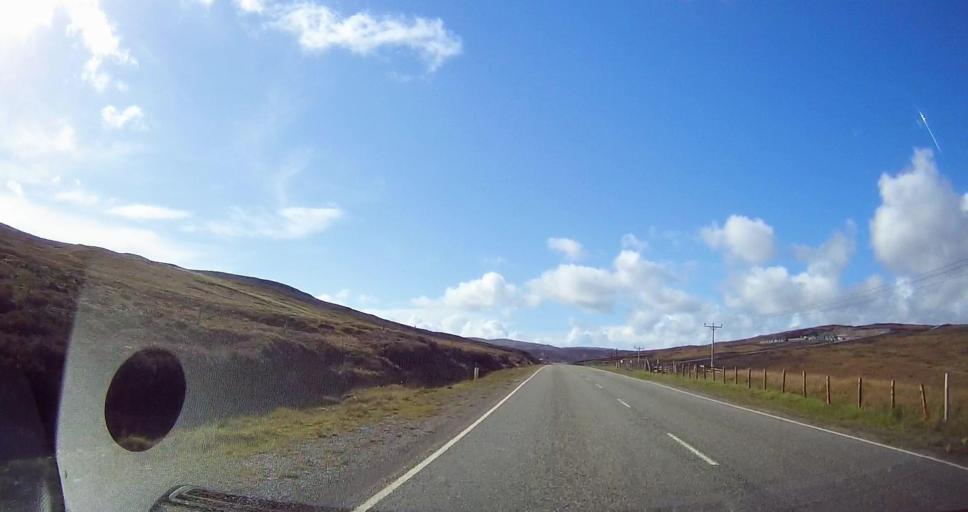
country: GB
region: Scotland
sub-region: Shetland Islands
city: Lerwick
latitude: 60.2698
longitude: -1.2343
